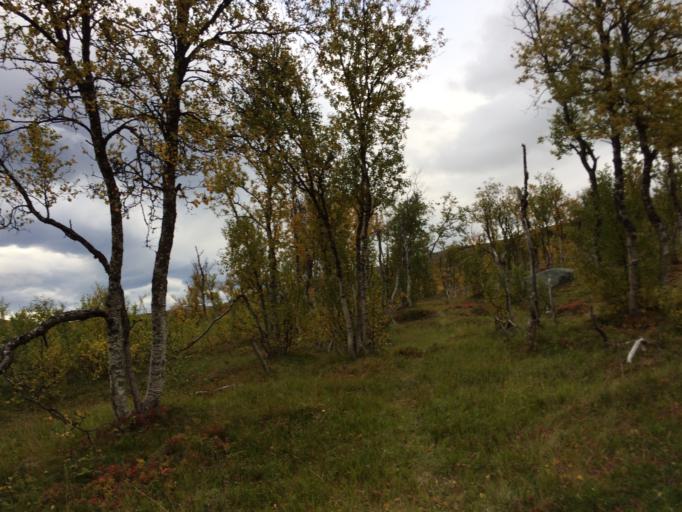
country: NO
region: Troms
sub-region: Sorreisa
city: Sorreisa
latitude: 69.5369
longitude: 18.3122
